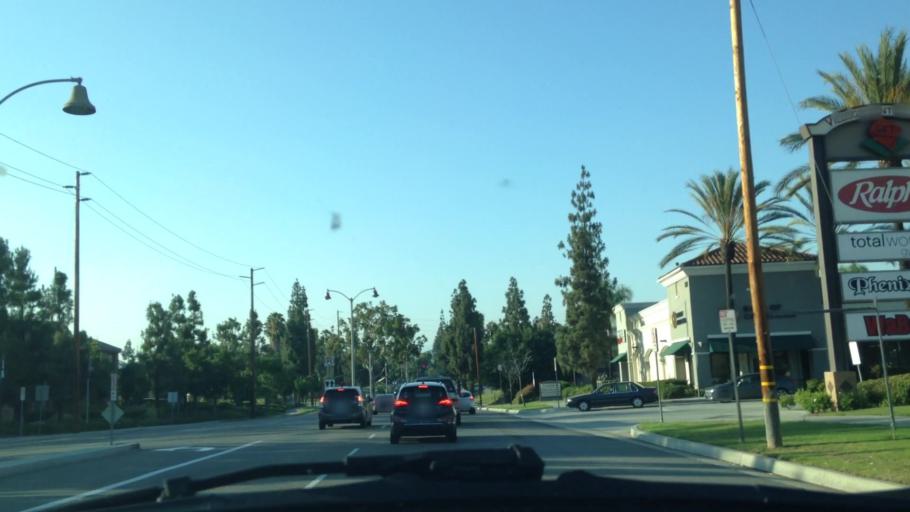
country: US
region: California
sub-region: Orange County
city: Placentia
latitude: 33.8777
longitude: -117.8434
